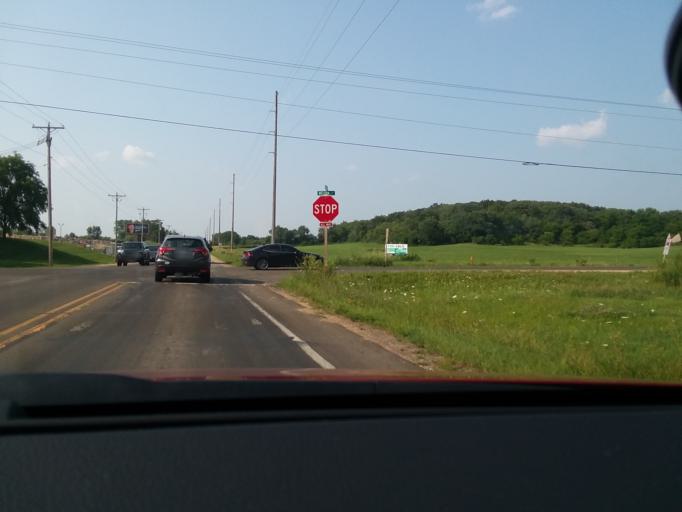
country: US
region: Wisconsin
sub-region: Dane County
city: Sun Prairie
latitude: 43.1429
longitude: -89.2659
